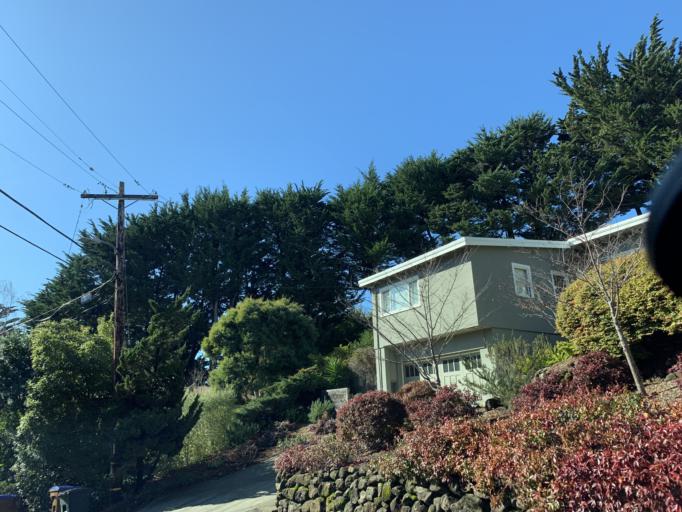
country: US
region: California
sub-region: Marin County
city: Strawberry
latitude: 37.8999
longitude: -122.5112
